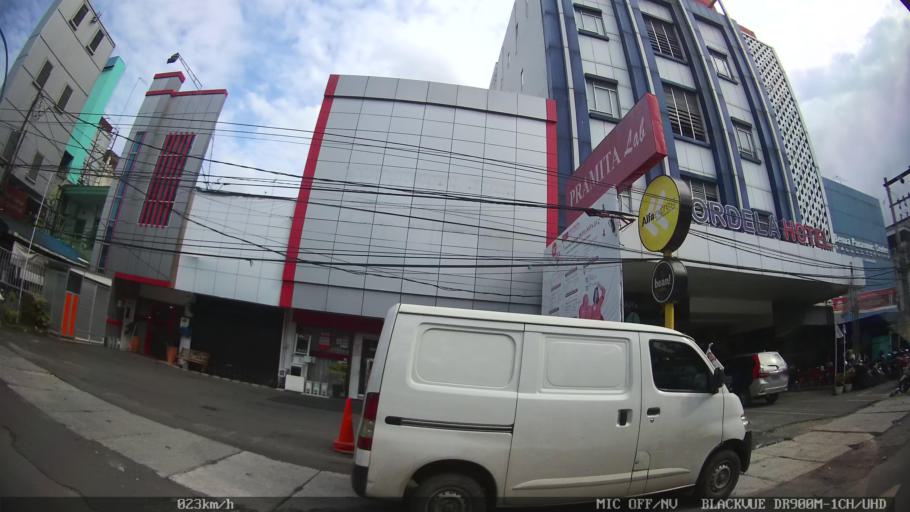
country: ID
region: North Sumatra
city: Medan
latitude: 3.5968
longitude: 98.6872
